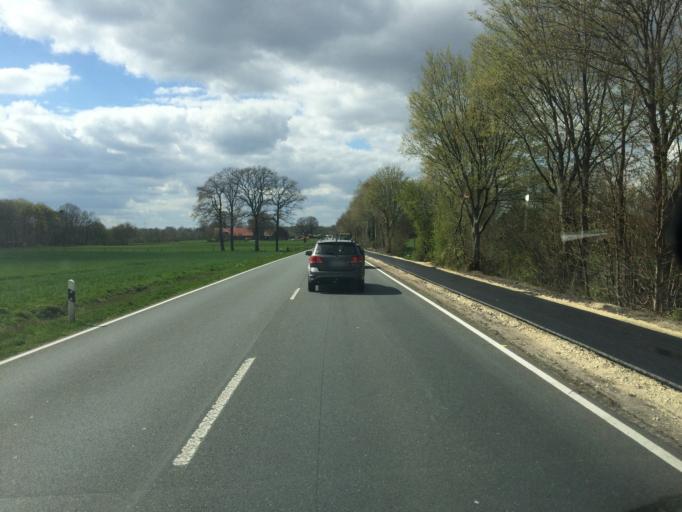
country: DE
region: North Rhine-Westphalia
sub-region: Regierungsbezirk Munster
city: Gescher
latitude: 51.9369
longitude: 7.0570
